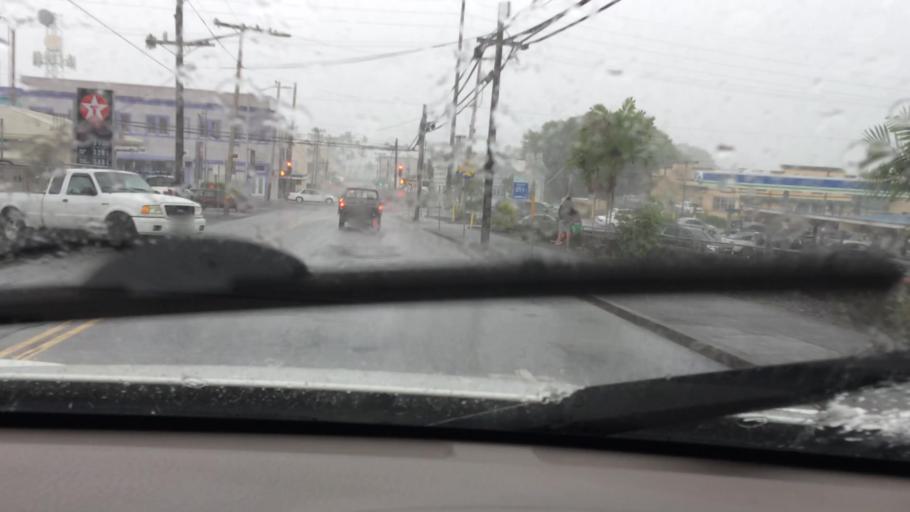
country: US
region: Hawaii
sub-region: Hawaii County
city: Hilo
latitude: 19.7231
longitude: -155.0886
